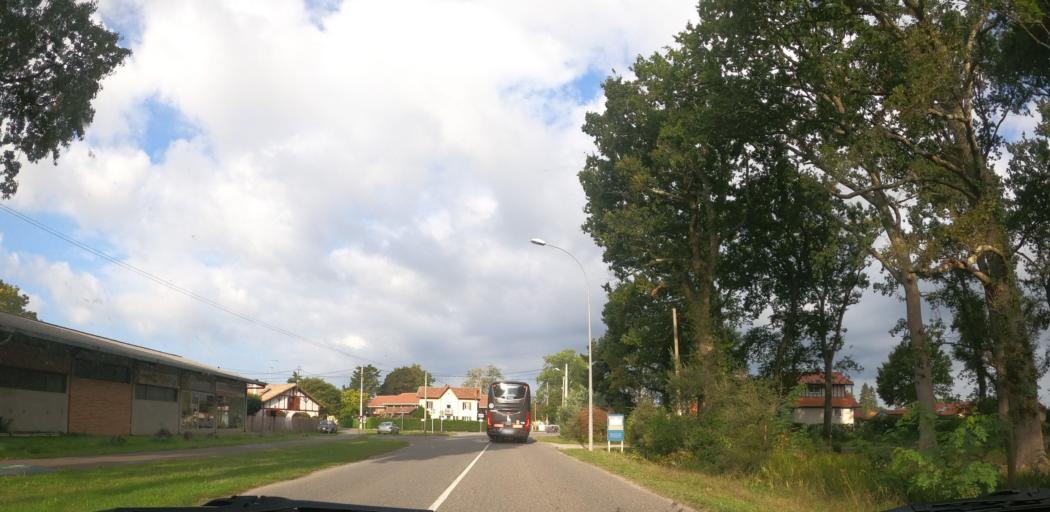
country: FR
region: Aquitaine
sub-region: Departement des Landes
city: Soustons
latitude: 43.7500
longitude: -1.3207
